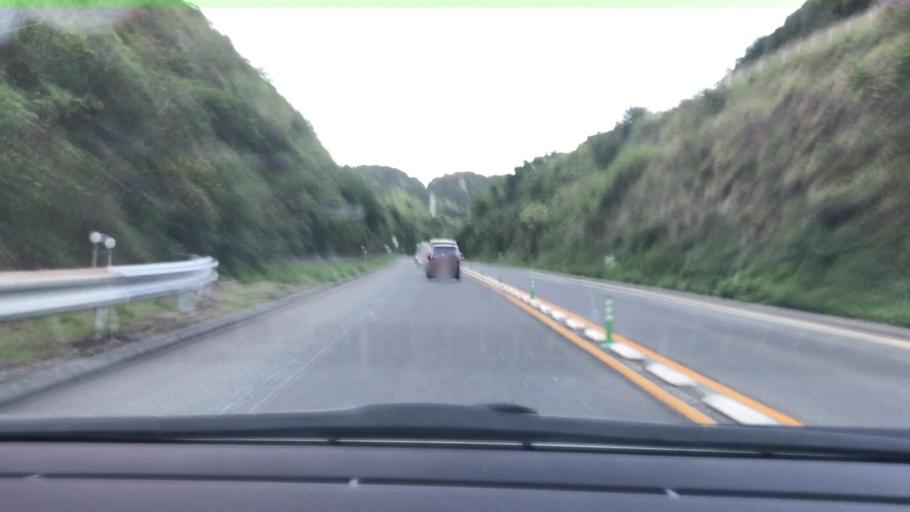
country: JP
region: Hiroshima
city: Innoshima
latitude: 34.3419
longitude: 133.1617
